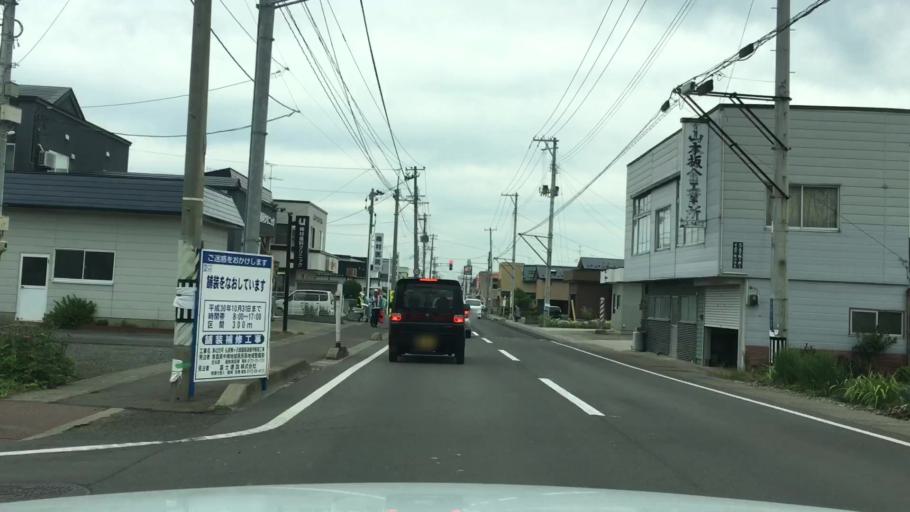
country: JP
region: Aomori
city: Hirosaki
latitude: 40.6261
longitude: 140.4553
